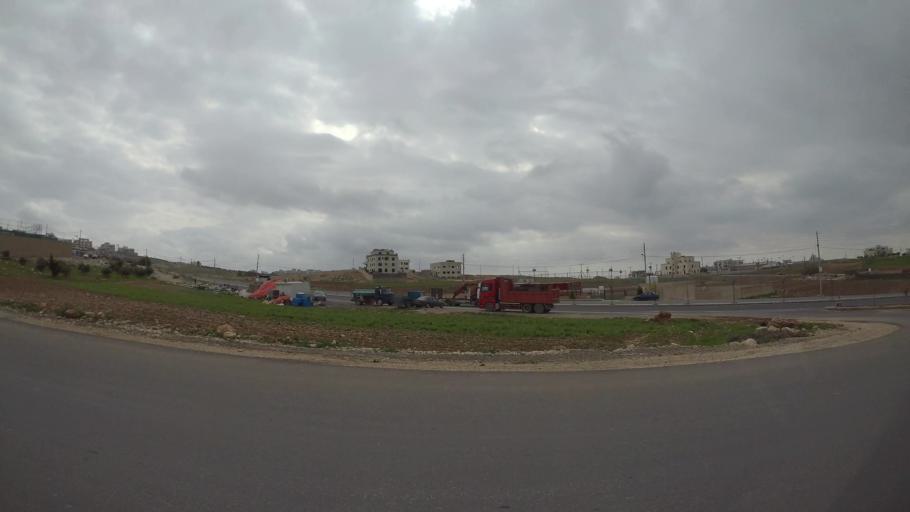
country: JO
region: Amman
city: Wadi as Sir
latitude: 31.9321
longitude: 35.8484
